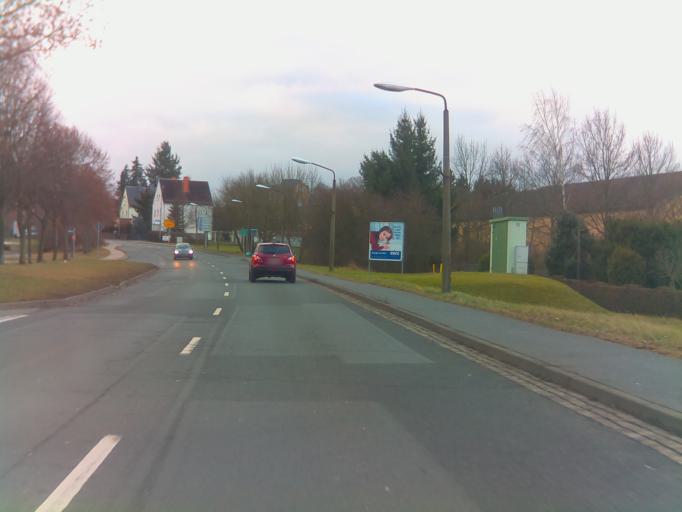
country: DE
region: Thuringia
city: Zeulenroda
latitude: 50.6553
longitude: 11.9761
